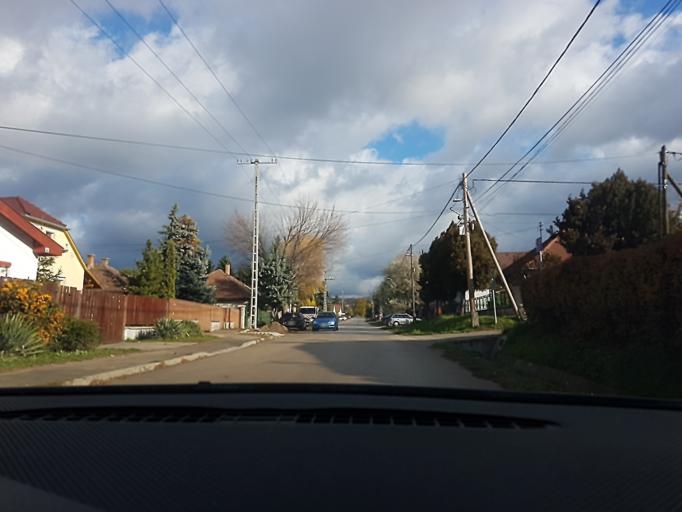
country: HU
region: Pest
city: Szada
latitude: 47.6313
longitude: 19.3038
